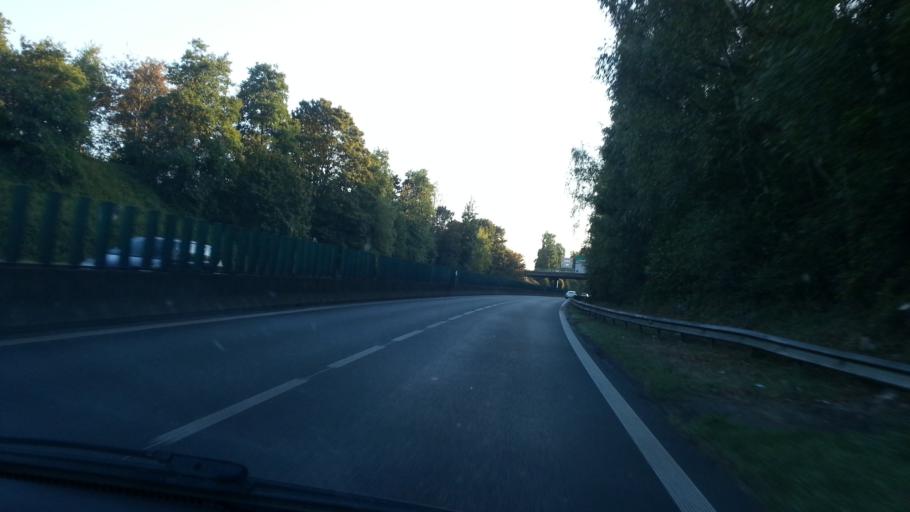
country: FR
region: Picardie
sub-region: Departement de l'Oise
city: Creil
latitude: 49.2567
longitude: 2.4923
